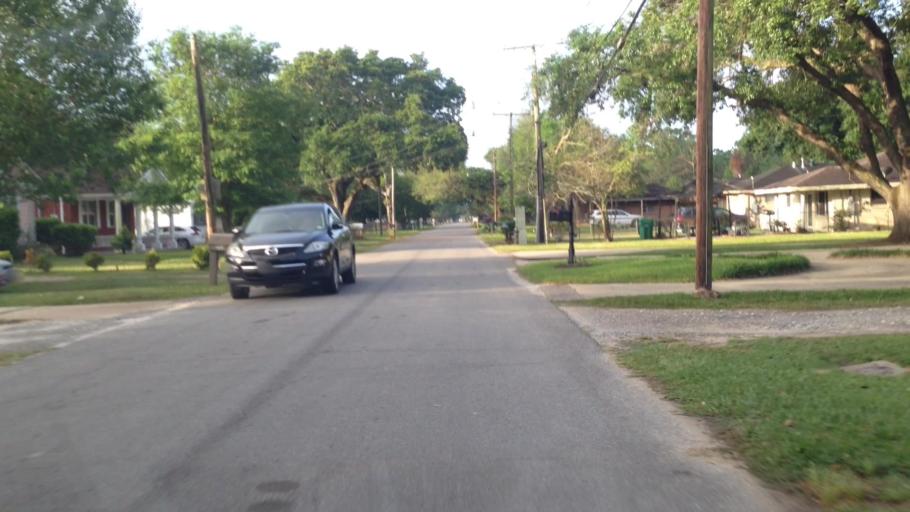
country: US
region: Louisiana
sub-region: Jefferson Parish
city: Bridge City
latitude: 29.9400
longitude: -90.1553
